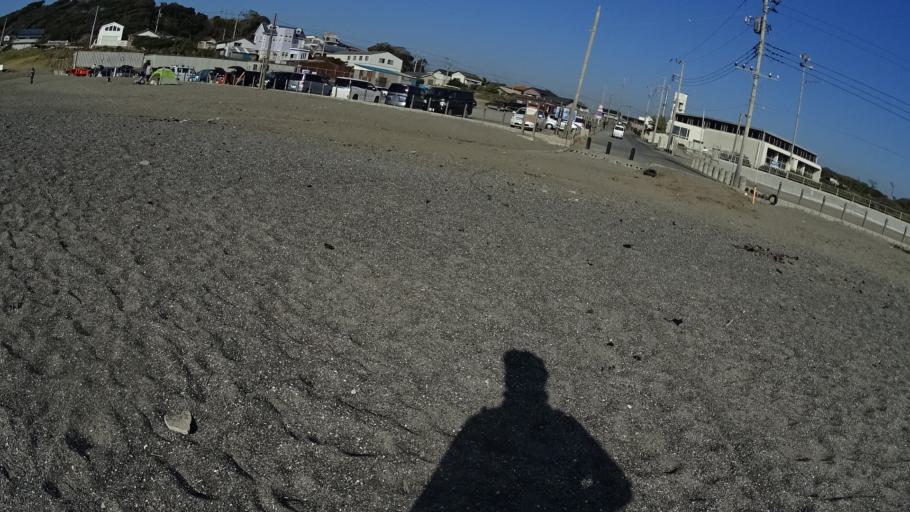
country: JP
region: Kanagawa
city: Miura
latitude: 35.1901
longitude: 139.6161
